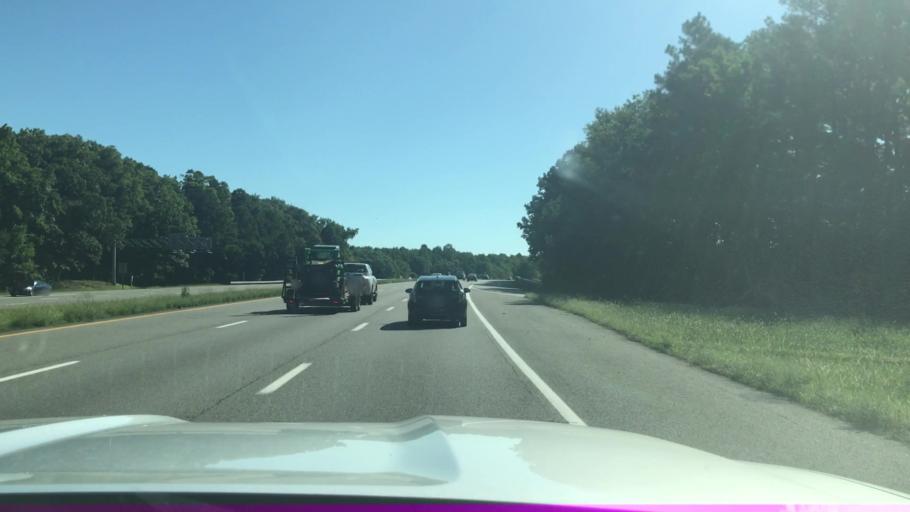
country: US
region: Virginia
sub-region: Henrico County
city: Montrose
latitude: 37.5323
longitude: -77.3582
